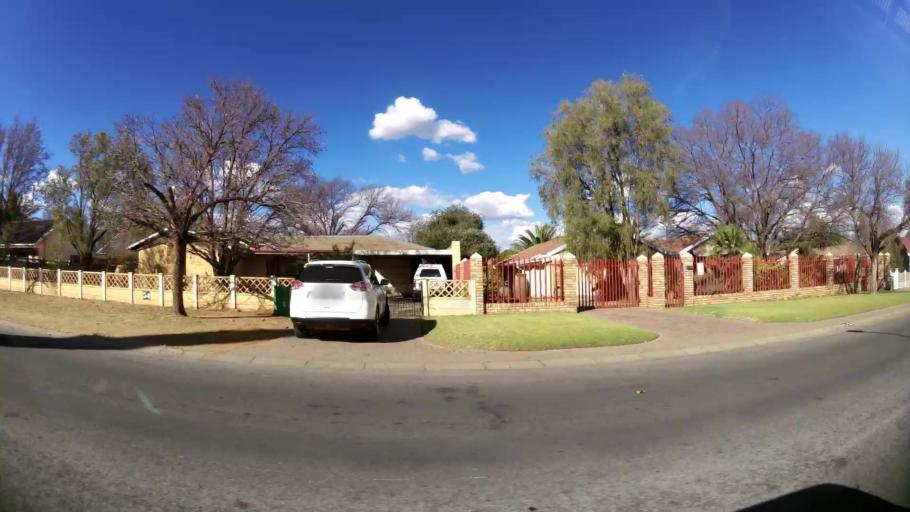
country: ZA
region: North-West
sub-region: Dr Kenneth Kaunda District Municipality
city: Klerksdorp
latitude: -26.8345
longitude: 26.6559
